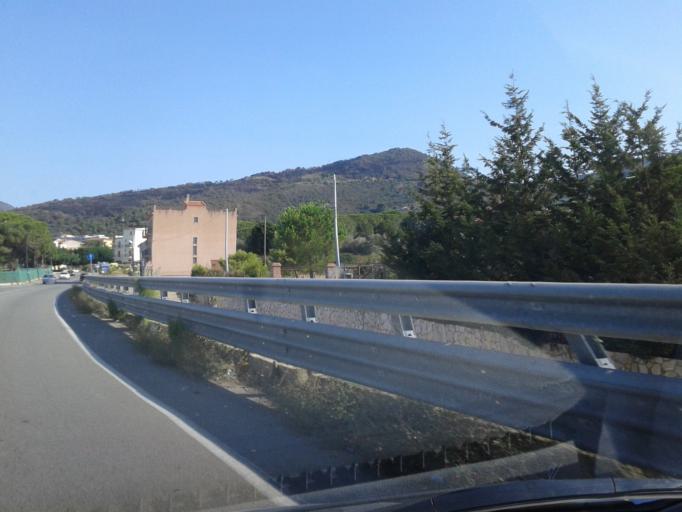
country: IT
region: Sicily
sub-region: Palermo
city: Finale
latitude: 38.0220
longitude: 14.1567
